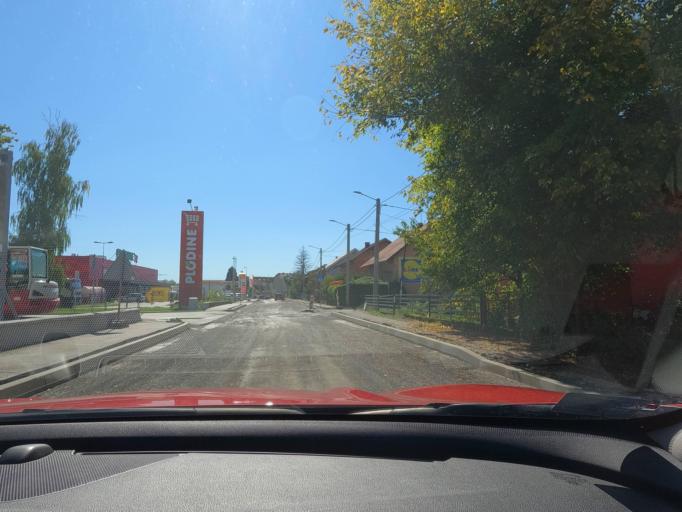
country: HR
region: Sisacko-Moslavacka
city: Petrinja
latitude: 45.4419
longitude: 16.2676
